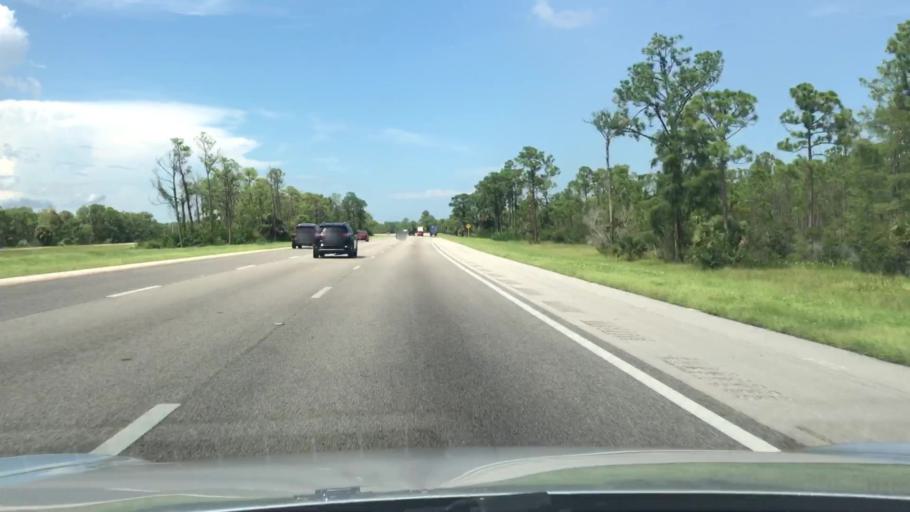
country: US
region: Florida
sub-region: Indian River County
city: Fellsmere
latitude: 27.8057
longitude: -80.5505
